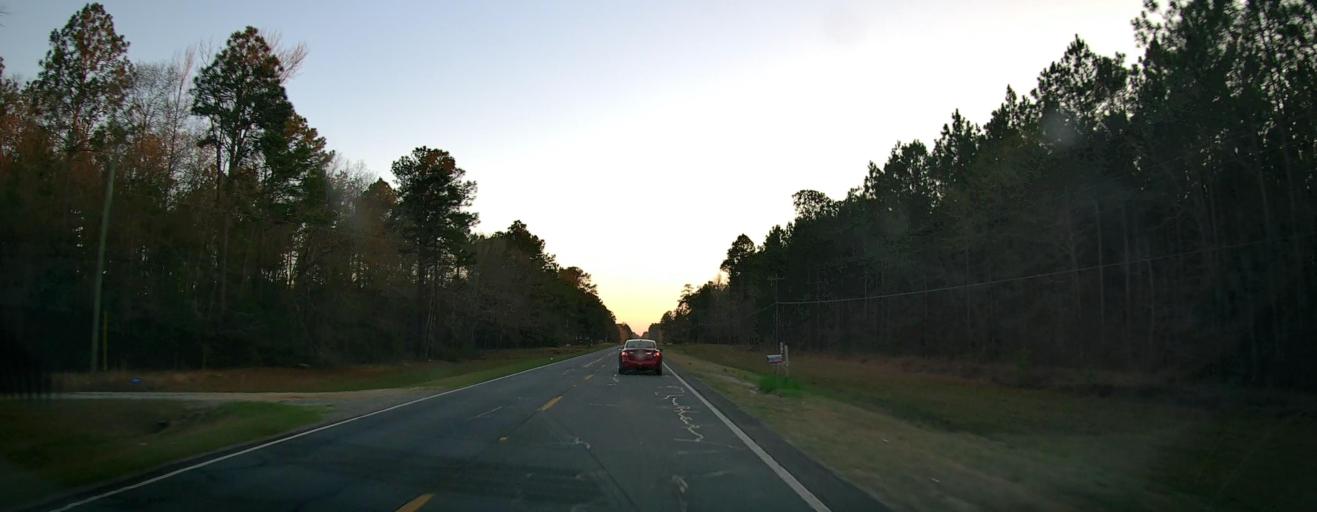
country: US
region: Georgia
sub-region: Dodge County
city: Eastman
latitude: 32.2440
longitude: -83.1454
